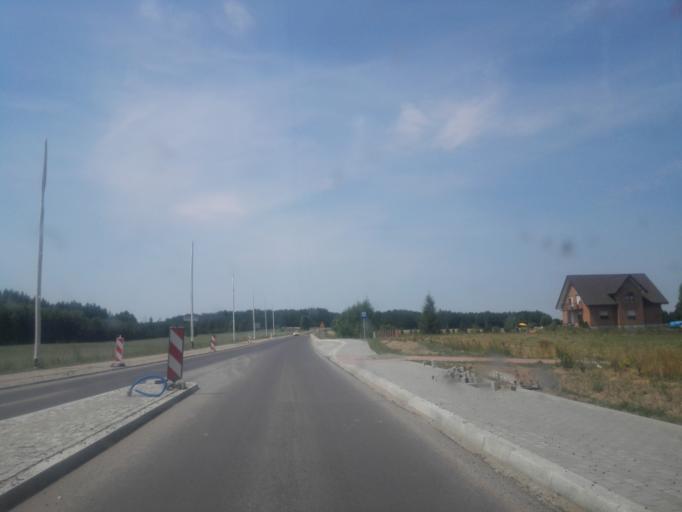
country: PL
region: Podlasie
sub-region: Powiat sejnenski
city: Krasnopol
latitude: 54.0817
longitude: 23.1142
